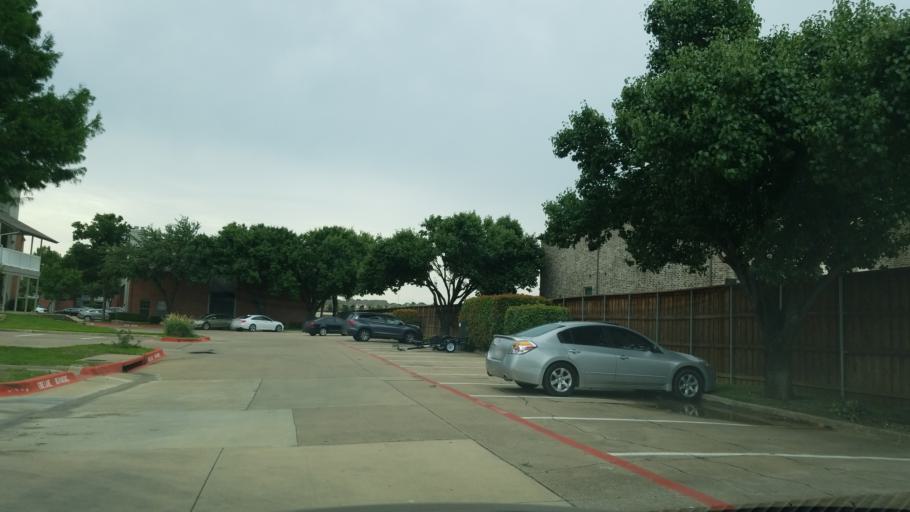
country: US
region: Texas
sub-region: Dallas County
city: Coppell
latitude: 32.9058
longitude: -96.9835
